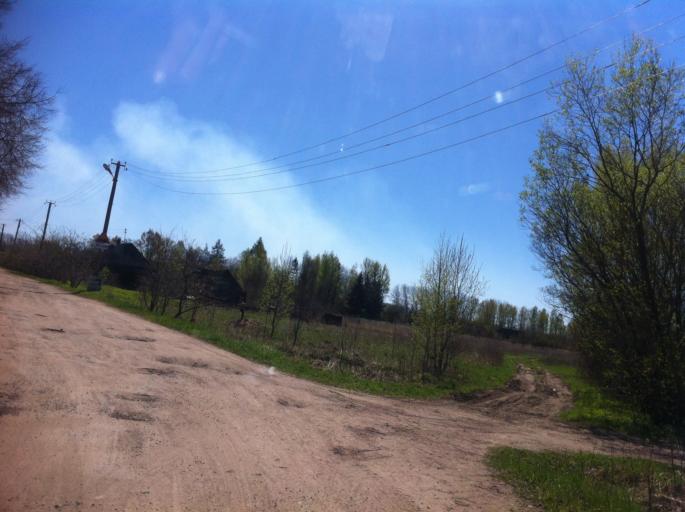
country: RU
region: Pskov
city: Izborsk
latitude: 57.7789
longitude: 27.9626
